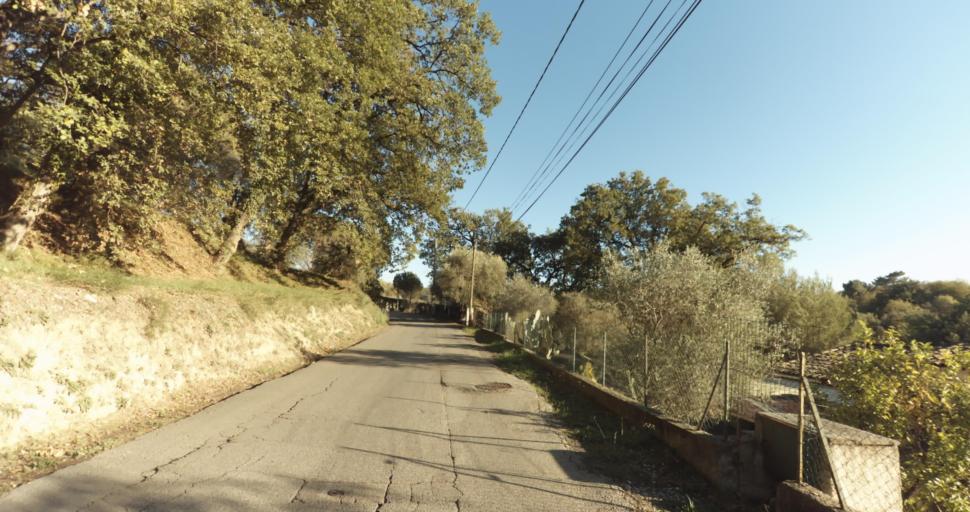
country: FR
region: Provence-Alpes-Cote d'Azur
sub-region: Departement des Alpes-Maritimes
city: Vence
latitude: 43.7338
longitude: 7.1281
